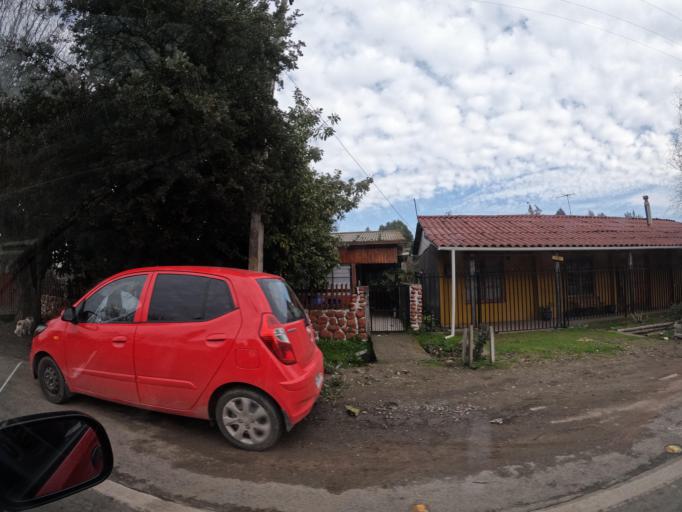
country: CL
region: Maule
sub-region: Provincia de Linares
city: Linares
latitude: -35.8604
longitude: -71.5706
